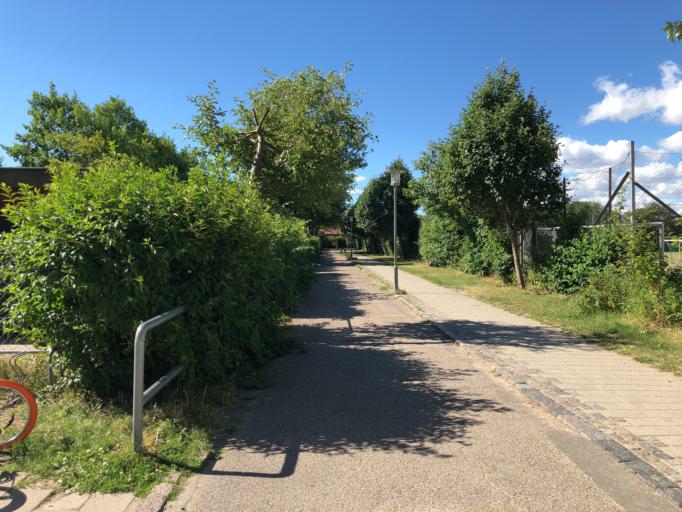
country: DK
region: Capital Region
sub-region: Gladsaxe Municipality
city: Buddinge
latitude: 55.7856
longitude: 12.4741
